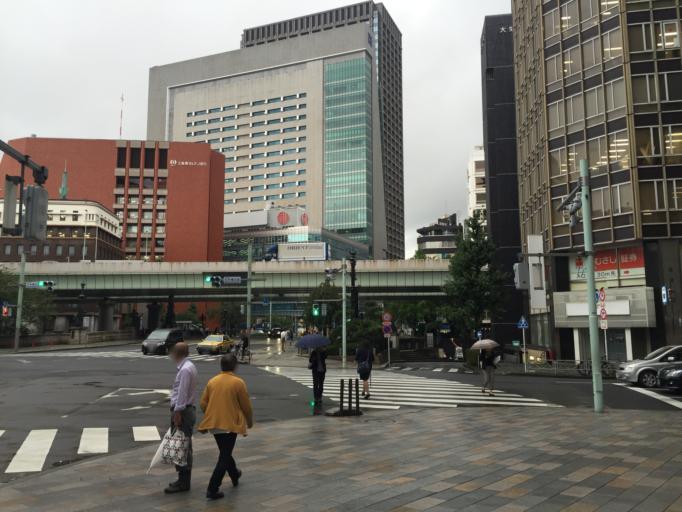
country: JP
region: Tokyo
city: Tokyo
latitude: 35.6851
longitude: 139.7745
